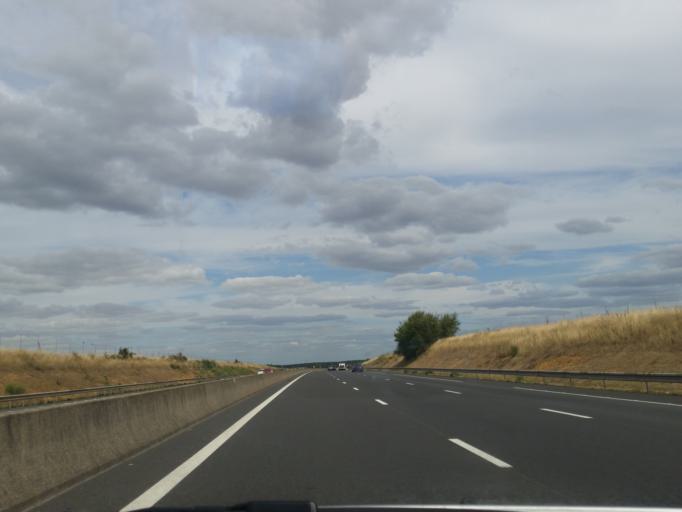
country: FR
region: Centre
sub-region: Departement d'Indre-et-Loire
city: Reugny
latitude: 47.5049
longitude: 0.8705
